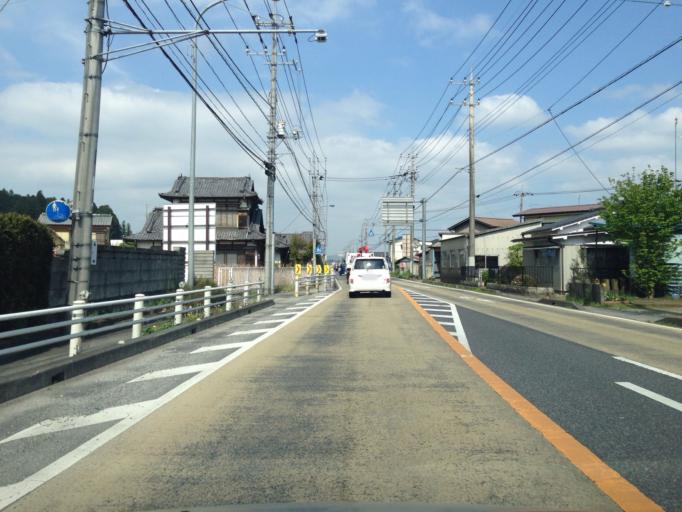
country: JP
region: Ibaraki
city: Kasama
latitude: 36.3711
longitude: 140.2128
